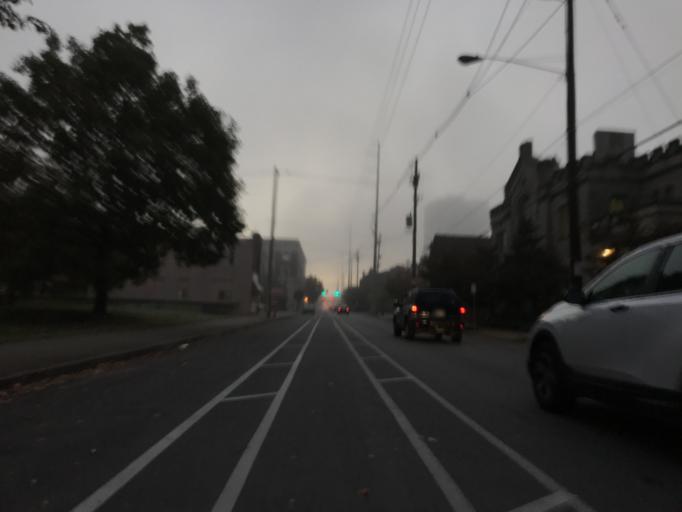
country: US
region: Kentucky
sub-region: Jefferson County
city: Louisville
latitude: 38.2389
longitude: -85.7594
